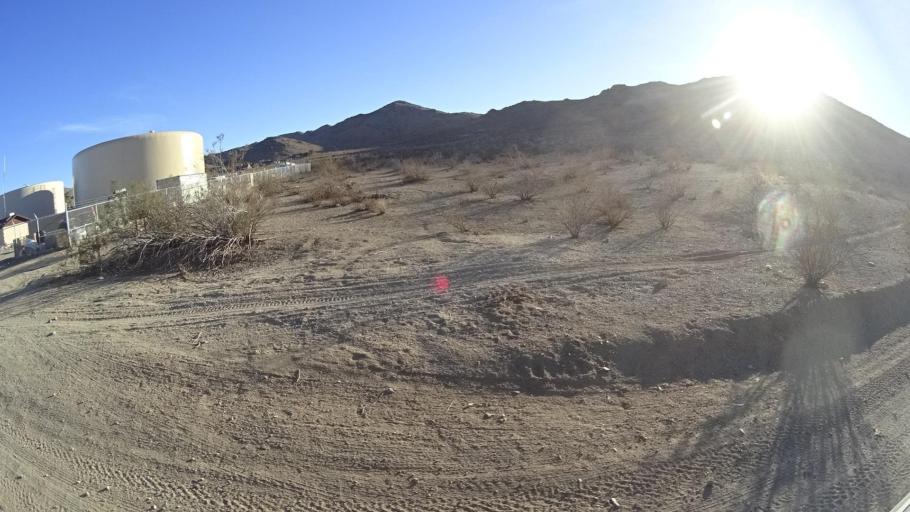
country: US
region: California
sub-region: Kern County
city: Ridgecrest
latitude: 35.5787
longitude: -117.6536
